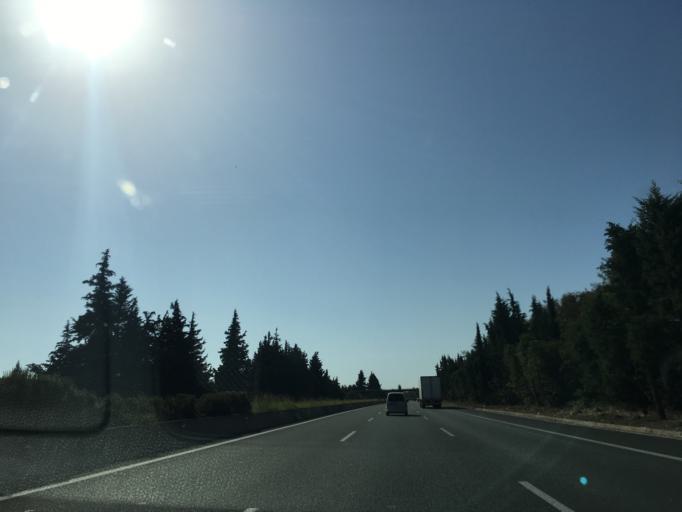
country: GR
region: Central Macedonia
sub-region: Nomos Pierias
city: Makrygialos
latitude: 40.3984
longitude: 22.6006
